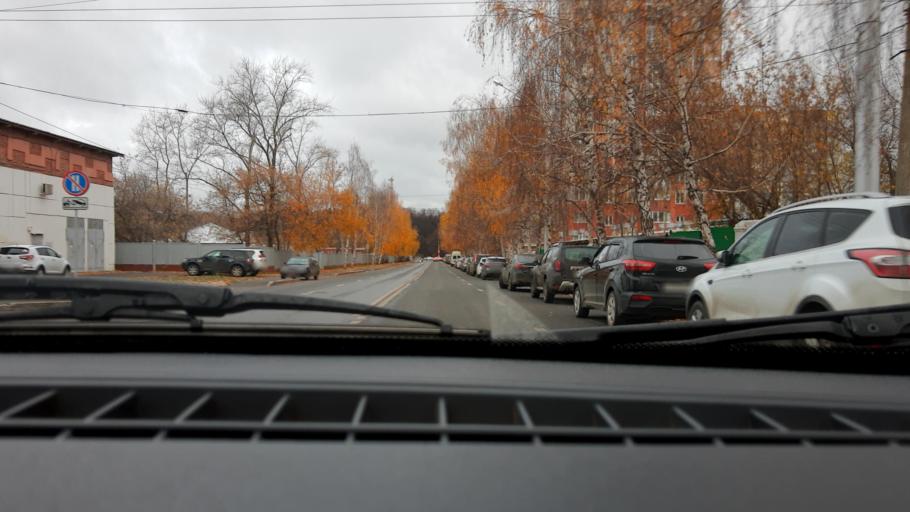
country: RU
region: Bashkortostan
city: Ufa
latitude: 54.7648
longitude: 56.0136
